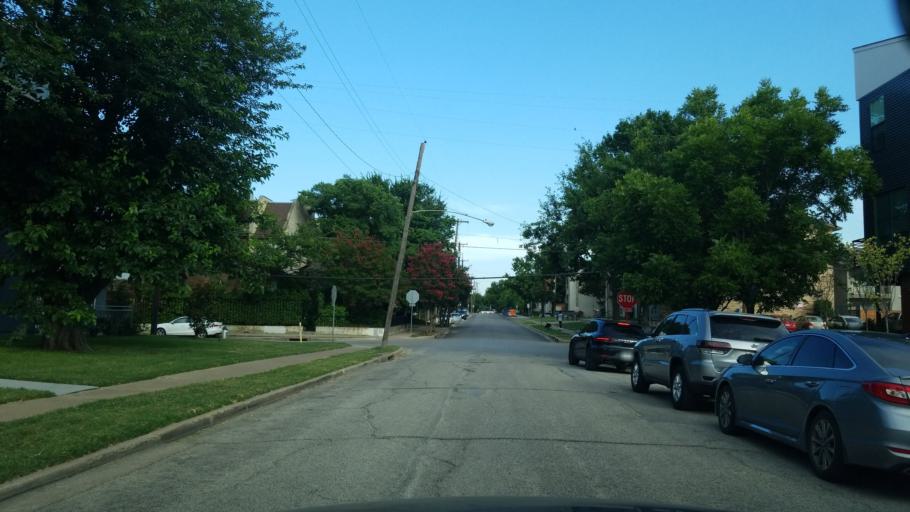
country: US
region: Texas
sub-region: Dallas County
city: Highland Park
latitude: 32.8114
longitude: -96.7784
